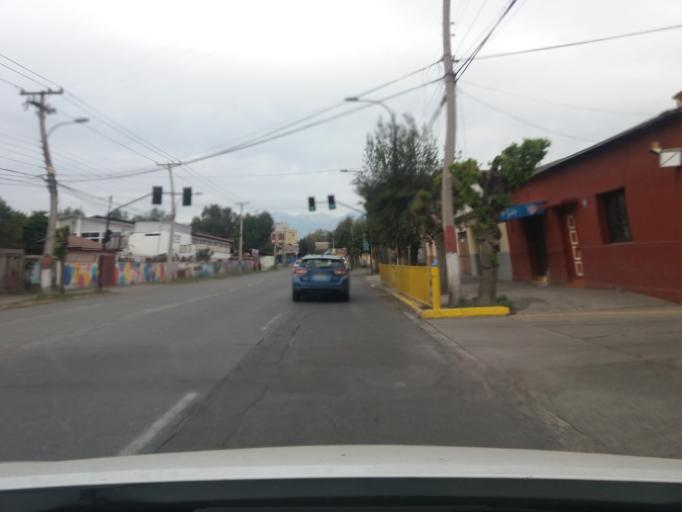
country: CL
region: Valparaiso
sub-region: Provincia de San Felipe
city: San Felipe
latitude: -32.7561
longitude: -70.7334
